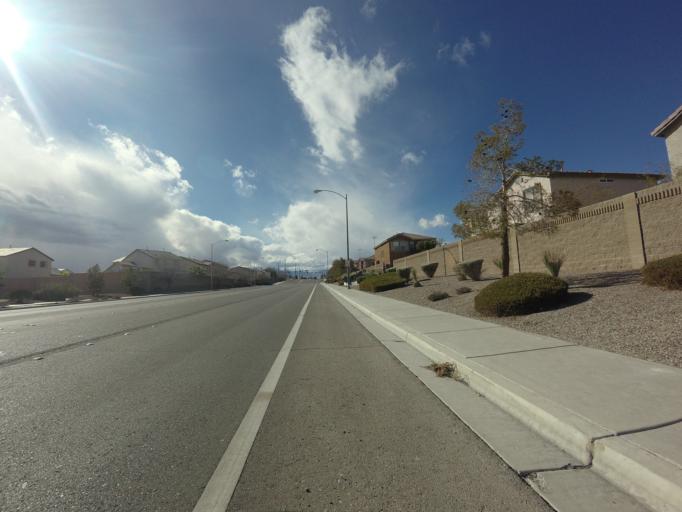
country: US
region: Nevada
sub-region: Clark County
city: North Las Vegas
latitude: 36.2543
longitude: -115.1321
